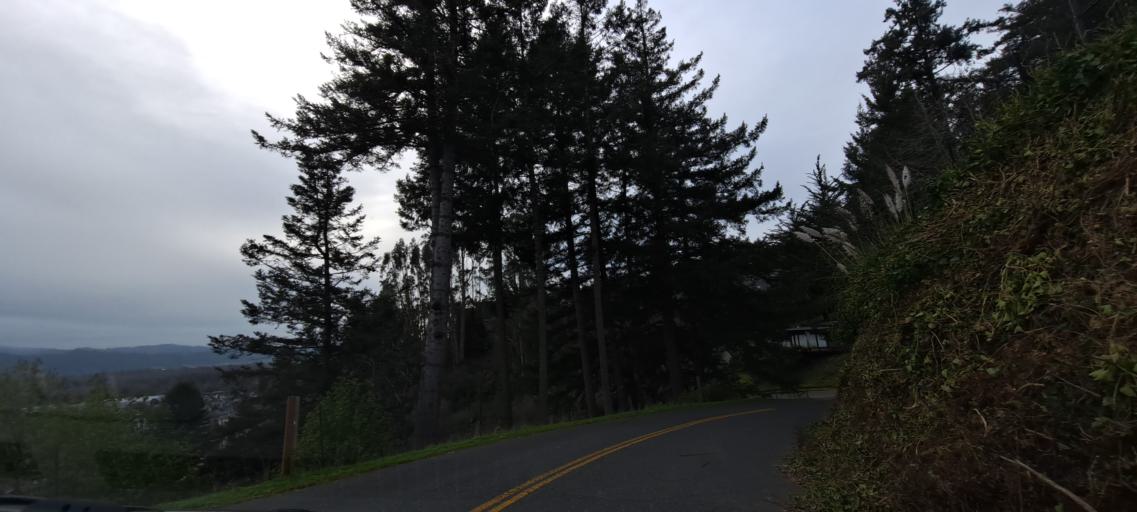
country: US
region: California
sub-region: Humboldt County
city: Fortuna
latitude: 40.6014
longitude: -124.1543
